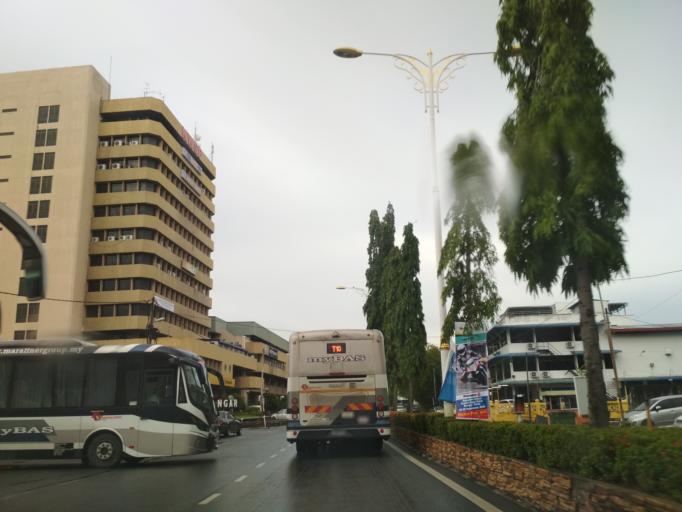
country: MY
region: Perlis
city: Kangar
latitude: 6.4351
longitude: 100.1927
